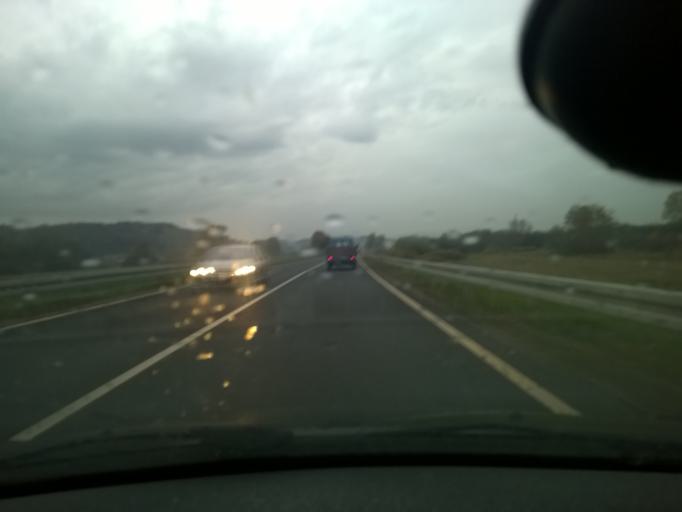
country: HR
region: Zagrebacka
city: Jakovlje
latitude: 45.9827
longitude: 15.8456
